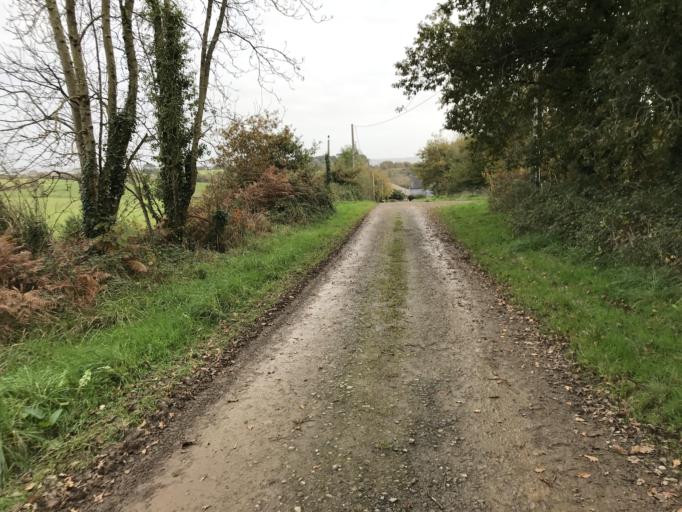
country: FR
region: Brittany
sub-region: Departement du Finistere
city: Hopital-Camfrout
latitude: 48.3302
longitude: -4.2075
